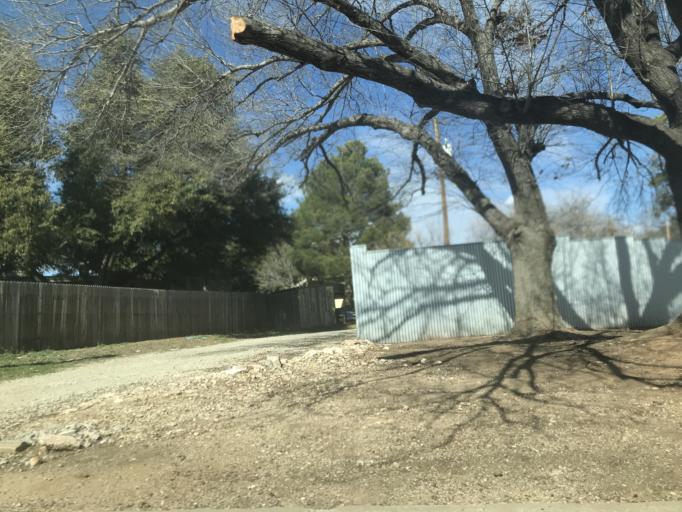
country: US
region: Texas
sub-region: Tom Green County
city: San Angelo
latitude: 31.4408
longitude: -100.4732
